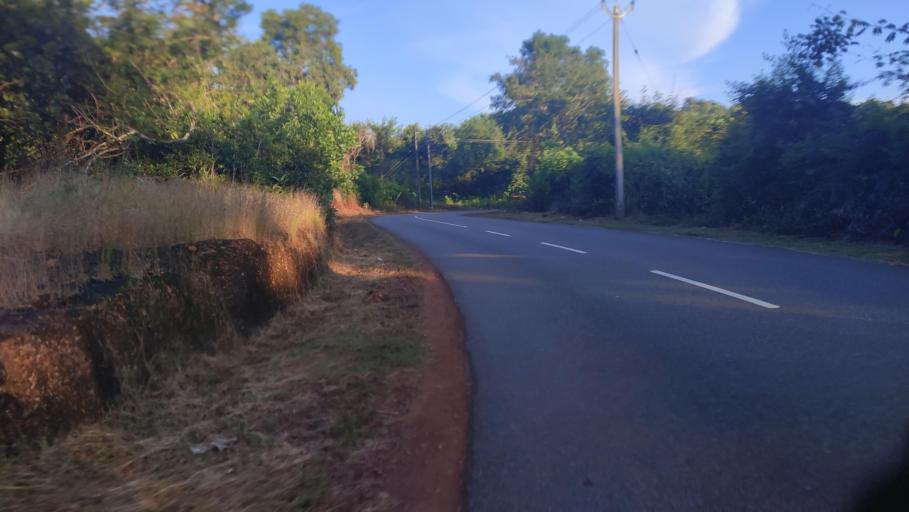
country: IN
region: Kerala
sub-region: Kasaragod District
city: Kasaragod
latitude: 12.4526
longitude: 75.0985
